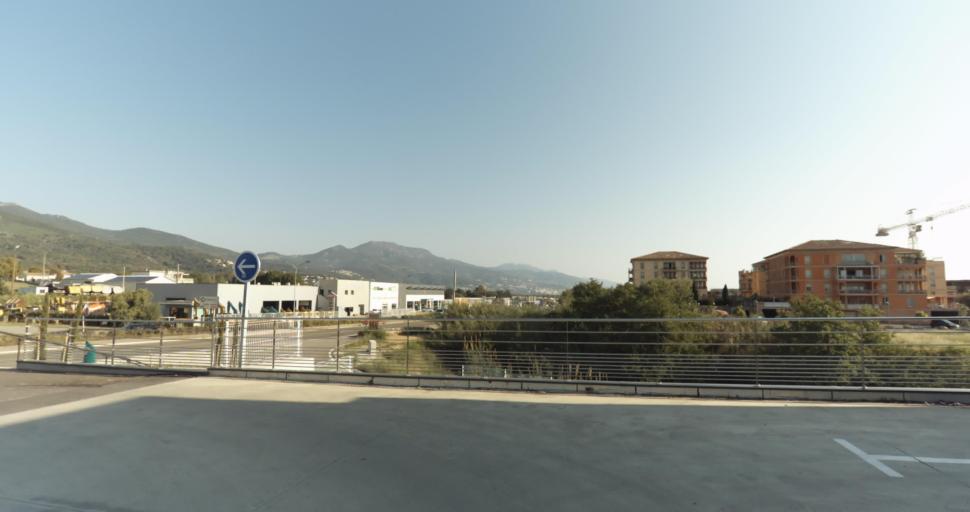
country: FR
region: Corsica
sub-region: Departement de la Haute-Corse
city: Biguglia
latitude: 42.6249
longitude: 9.4374
